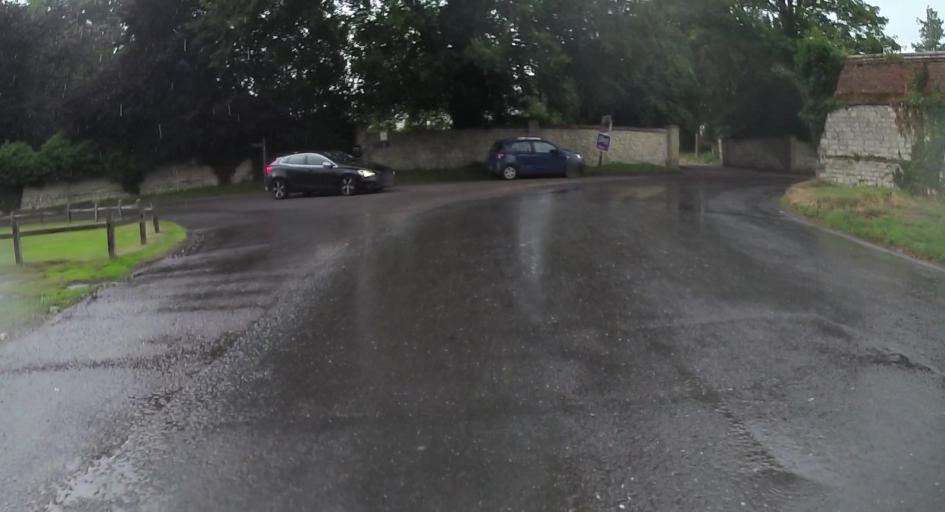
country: GB
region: England
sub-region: Hampshire
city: Long Sutton
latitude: 51.1784
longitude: -0.9230
